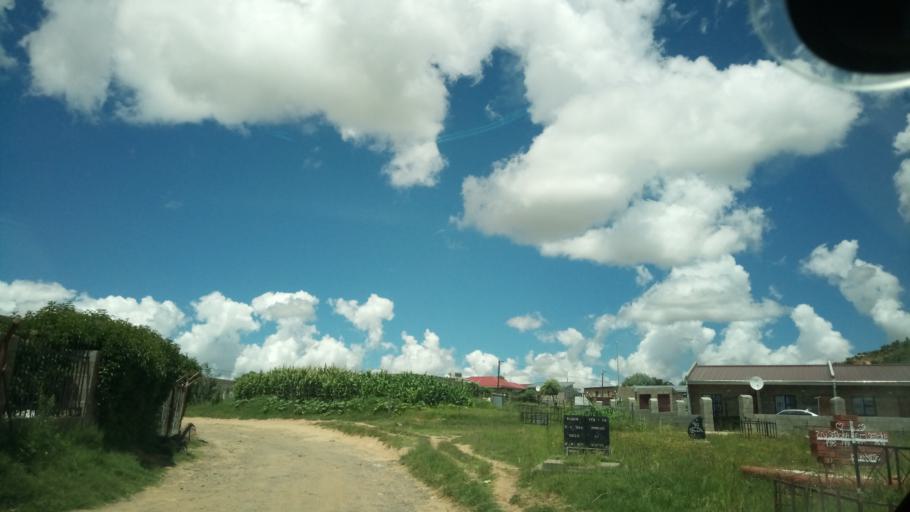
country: LS
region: Maseru
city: Maseru
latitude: -29.3651
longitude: 27.5414
